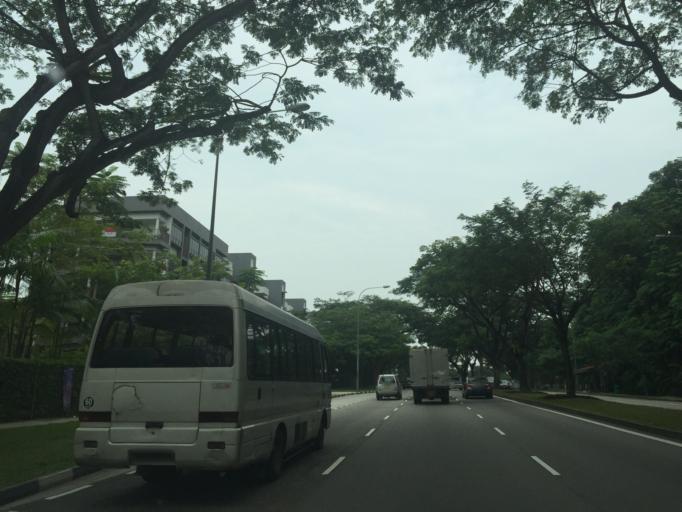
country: SG
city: Singapore
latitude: 1.3799
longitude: 103.8274
